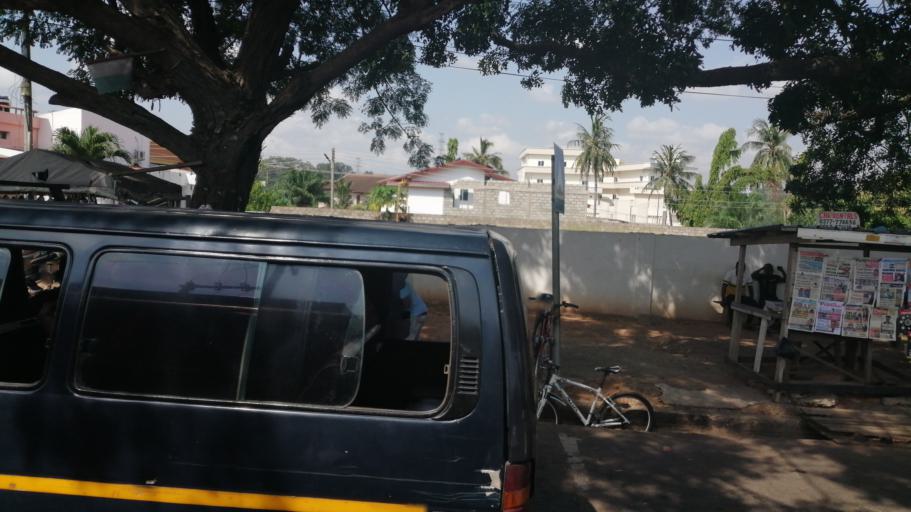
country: GH
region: Greater Accra
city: Medina Estates
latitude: 5.6357
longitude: -0.1720
